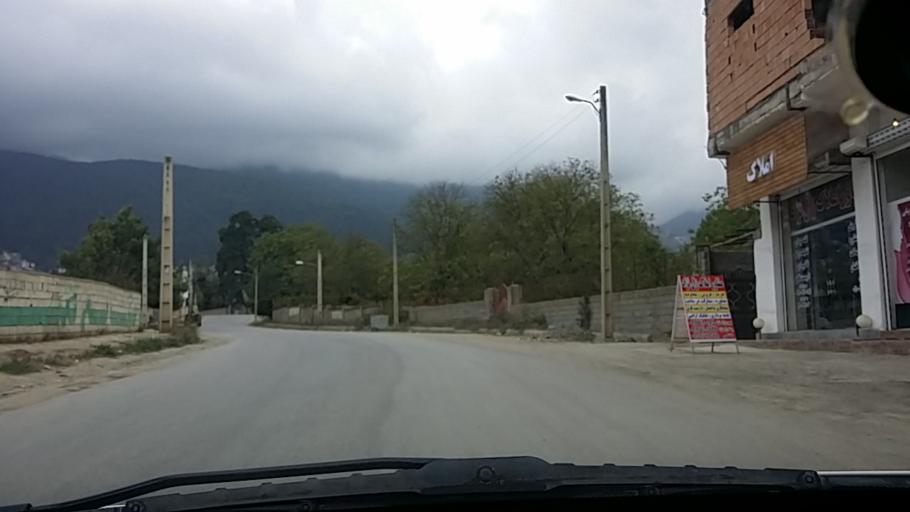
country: IR
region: Mazandaran
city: `Abbasabad
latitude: 36.5055
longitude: 51.1636
